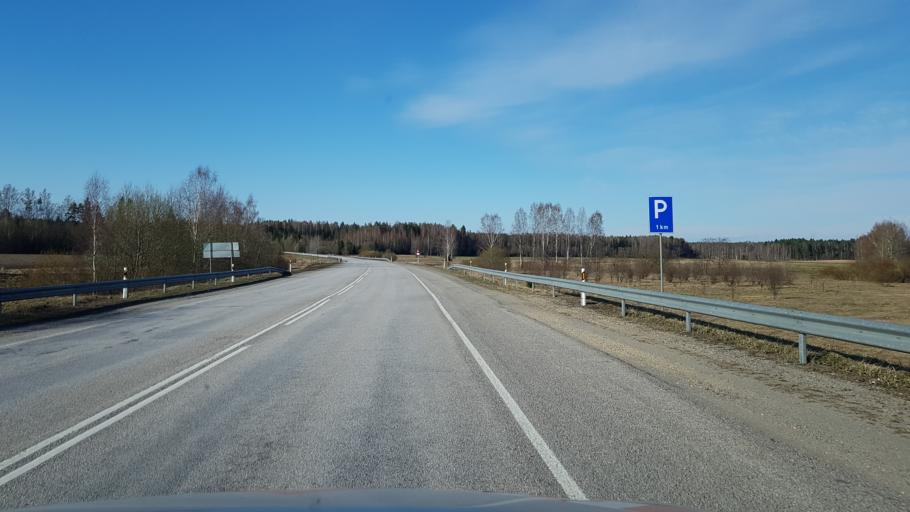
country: EE
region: Ida-Virumaa
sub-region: Johvi vald
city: Johvi
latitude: 59.1471
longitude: 27.3583
